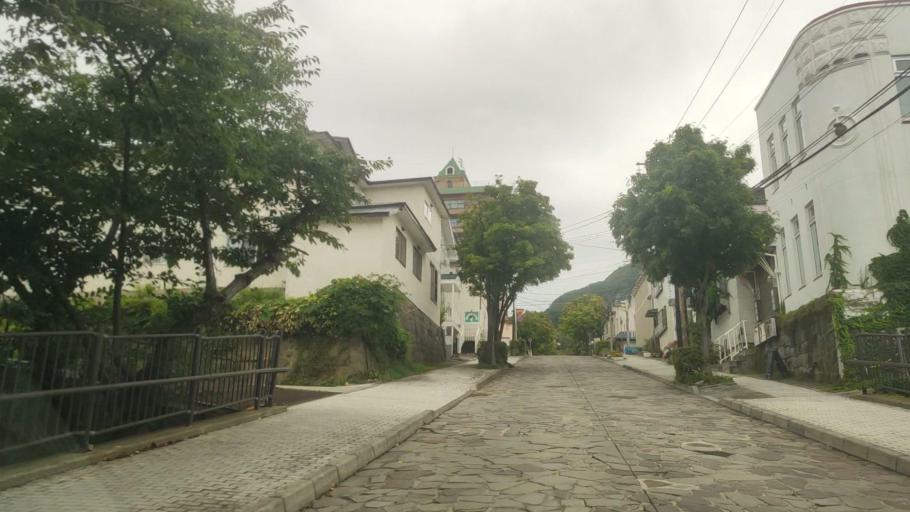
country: JP
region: Hokkaido
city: Hakodate
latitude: 41.7647
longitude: 140.7150
